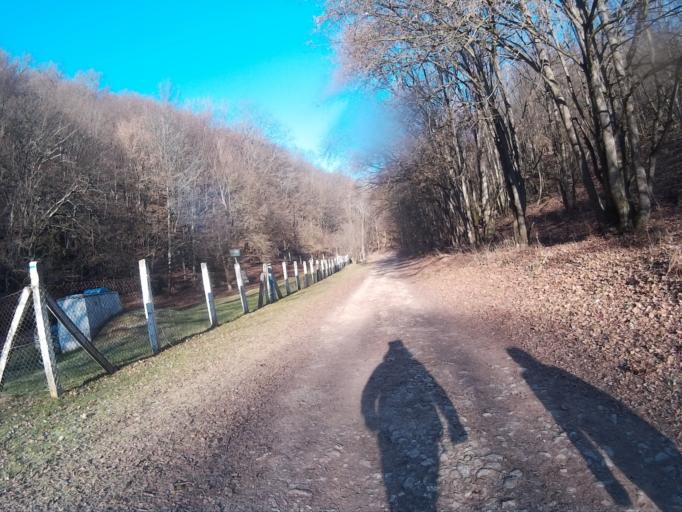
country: HU
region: Borsod-Abauj-Zemplen
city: Rudabanya
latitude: 48.4879
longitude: 20.5501
